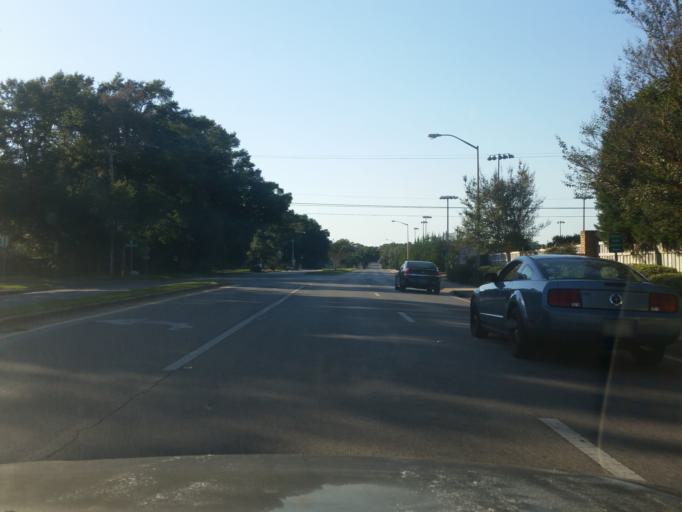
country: US
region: Florida
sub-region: Escambia County
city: Goulding
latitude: 30.4640
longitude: -87.1936
